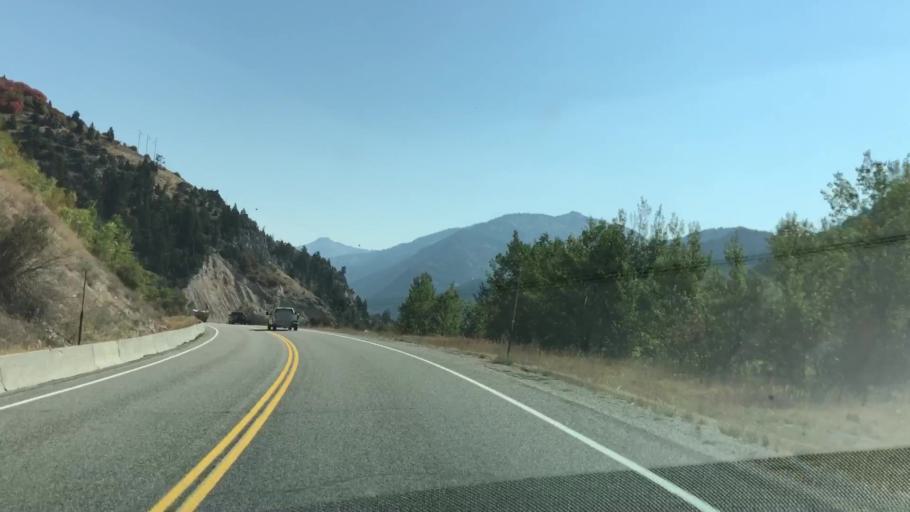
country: US
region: Idaho
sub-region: Teton County
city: Victor
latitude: 43.3188
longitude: -111.1525
